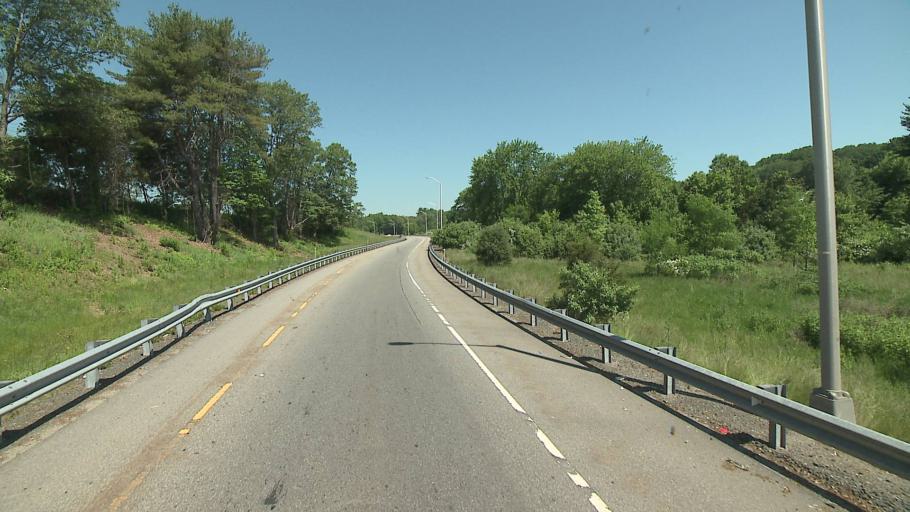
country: US
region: Connecticut
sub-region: New London County
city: Norwich
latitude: 41.5107
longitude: -72.1163
